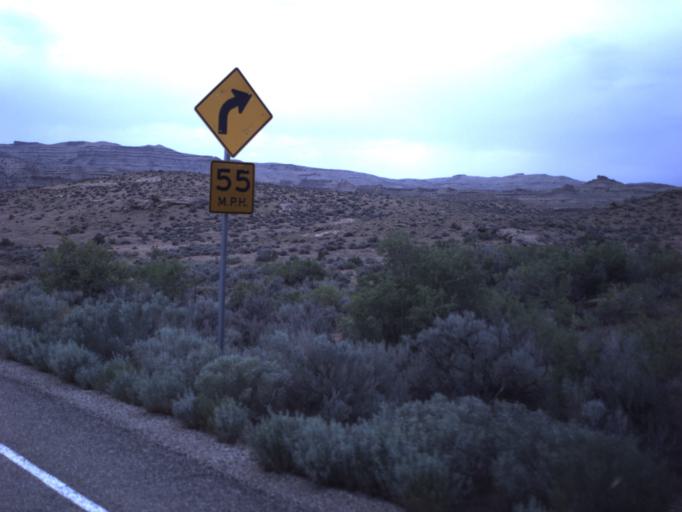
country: US
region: Colorado
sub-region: Rio Blanco County
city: Rangely
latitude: 39.9695
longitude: -109.1678
